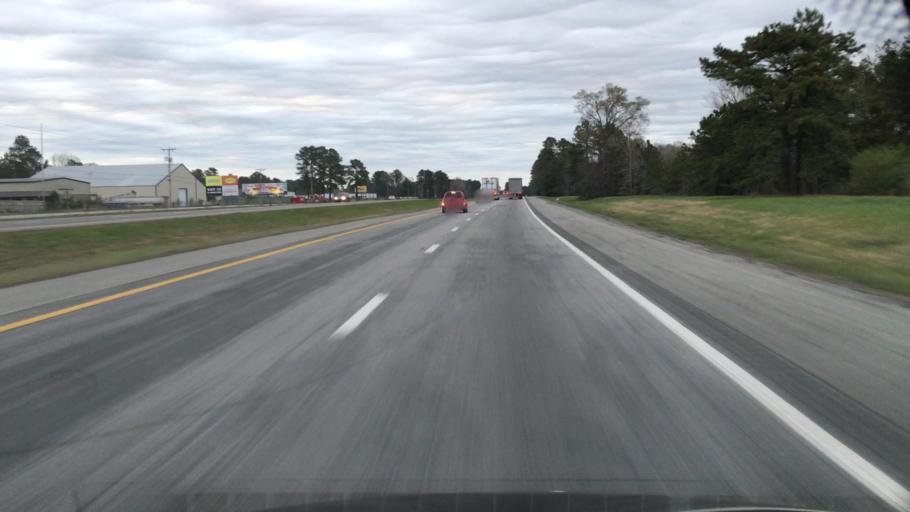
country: US
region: Virginia
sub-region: City of Emporia
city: Emporia
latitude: 36.8282
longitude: -77.4515
